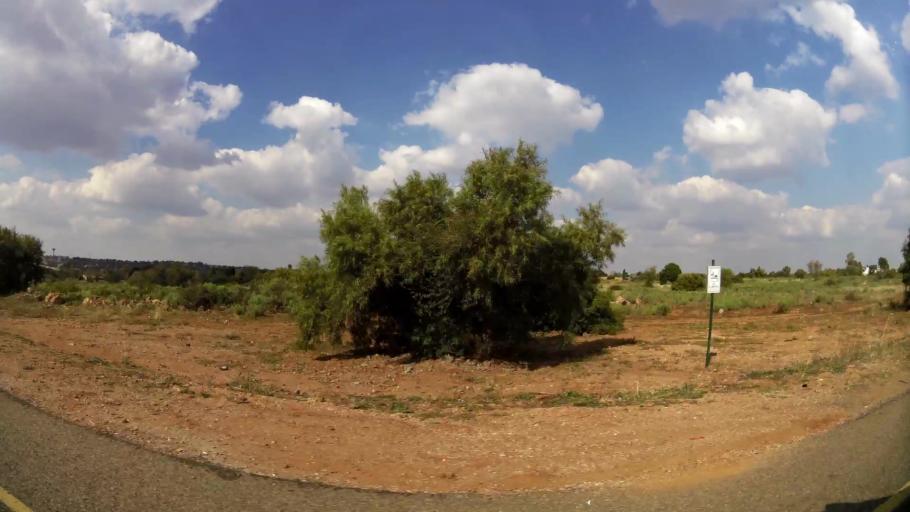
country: ZA
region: Gauteng
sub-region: City of Tshwane Metropolitan Municipality
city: Centurion
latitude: -25.8274
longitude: 28.2355
